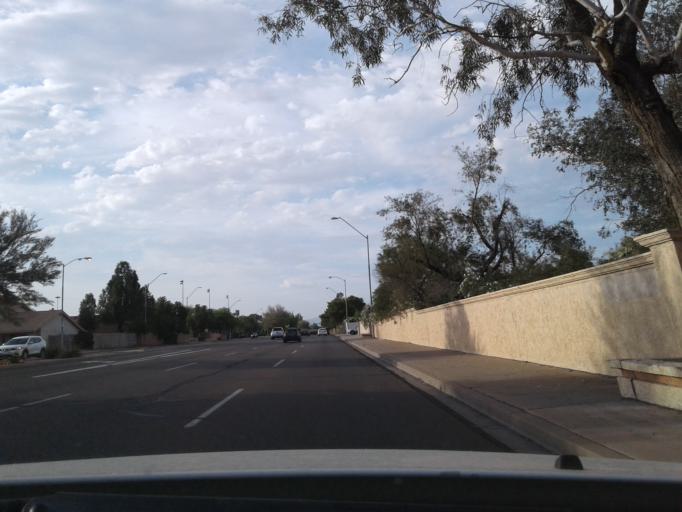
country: US
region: Arizona
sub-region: Maricopa County
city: Paradise Valley
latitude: 33.6142
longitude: -111.9777
